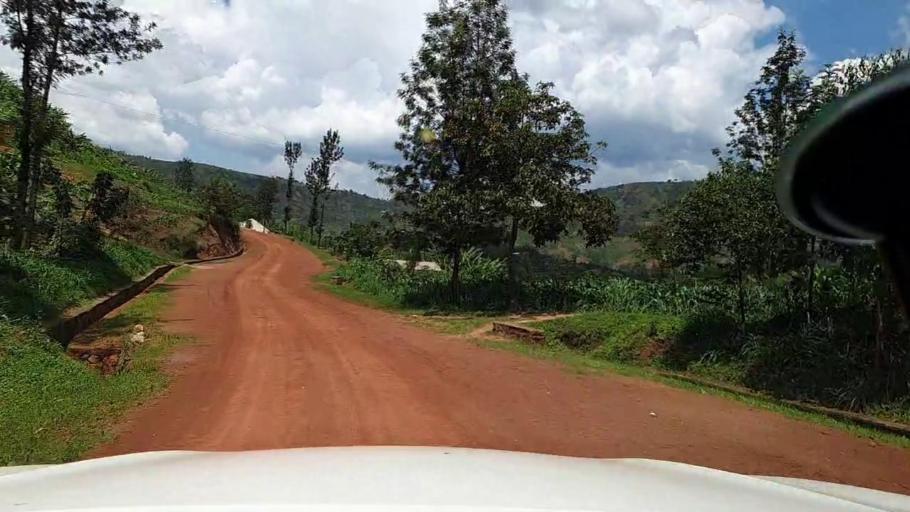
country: RW
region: Northern Province
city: Byumba
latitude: -1.6908
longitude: 29.8267
